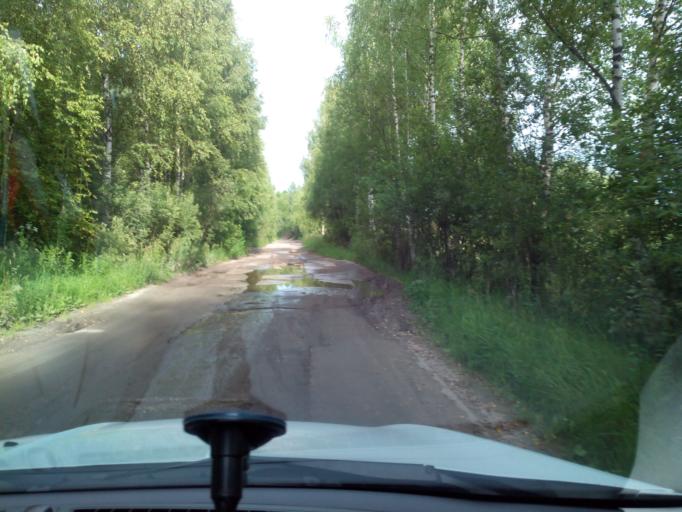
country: RU
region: Vladimir
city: Petushki
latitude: 56.0360
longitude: 39.5008
